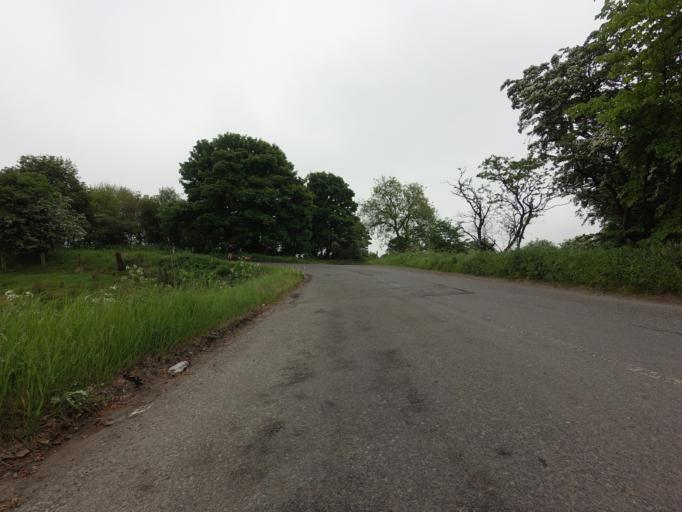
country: GB
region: Scotland
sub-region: Fife
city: Townhill
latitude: 56.0989
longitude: -3.4500
